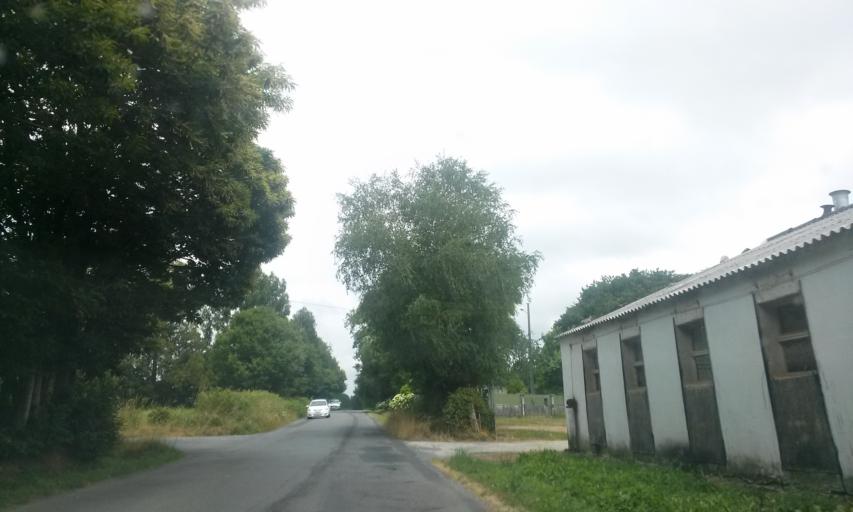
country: ES
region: Galicia
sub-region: Provincia de Lugo
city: Friol
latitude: 43.0926
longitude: -7.8091
